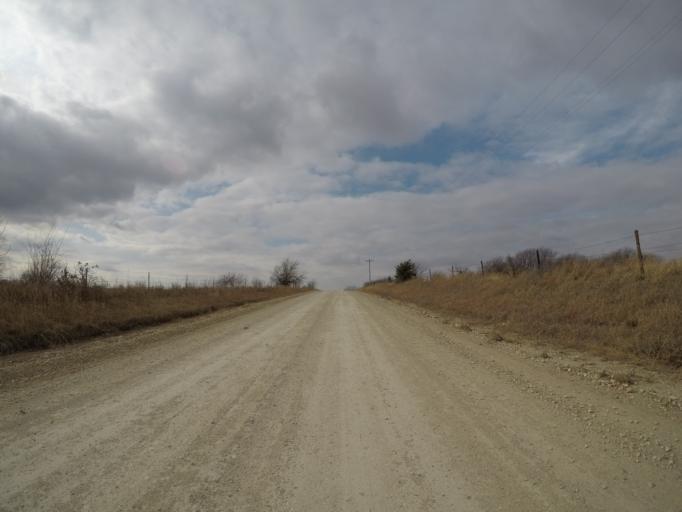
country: US
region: Kansas
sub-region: Morris County
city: Council Grove
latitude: 38.7680
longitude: -96.3039
